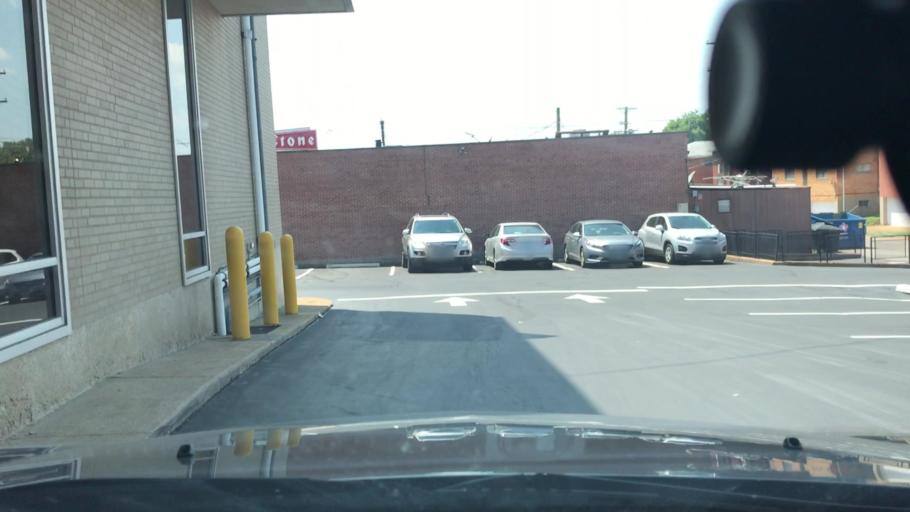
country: US
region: Missouri
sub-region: Saint Louis County
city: Maplewood
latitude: 38.5938
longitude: -90.2951
